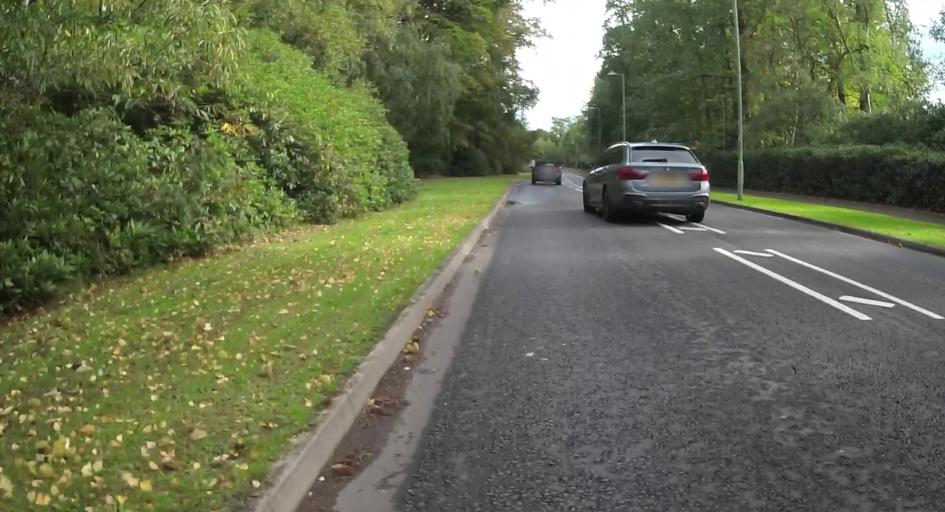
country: GB
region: England
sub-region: Hampshire
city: Fleet
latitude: 51.2977
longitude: -0.8348
